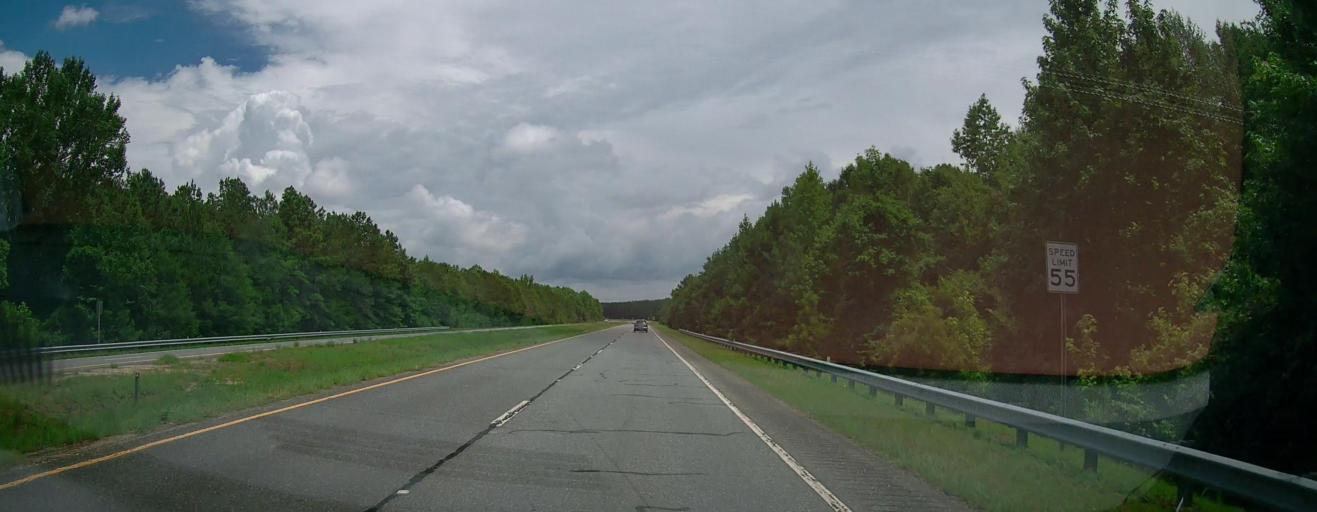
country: US
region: Georgia
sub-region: Dodge County
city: Eastman
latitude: 32.1845
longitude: -83.1980
